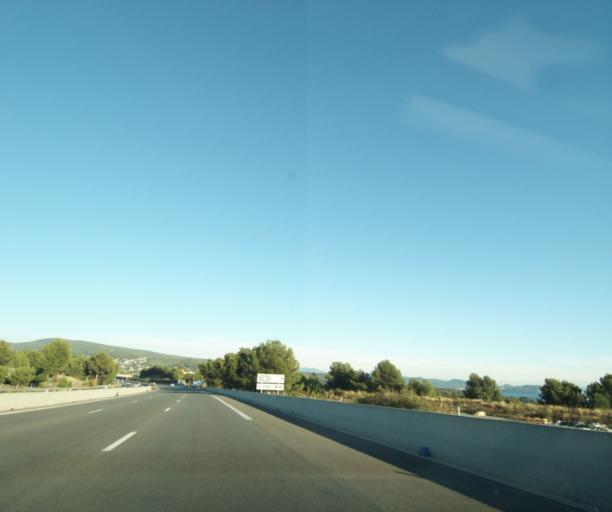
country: FR
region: Provence-Alpes-Cote d'Azur
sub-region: Departement des Bouches-du-Rhone
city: La Ciotat
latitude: 43.2033
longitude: 5.6021
